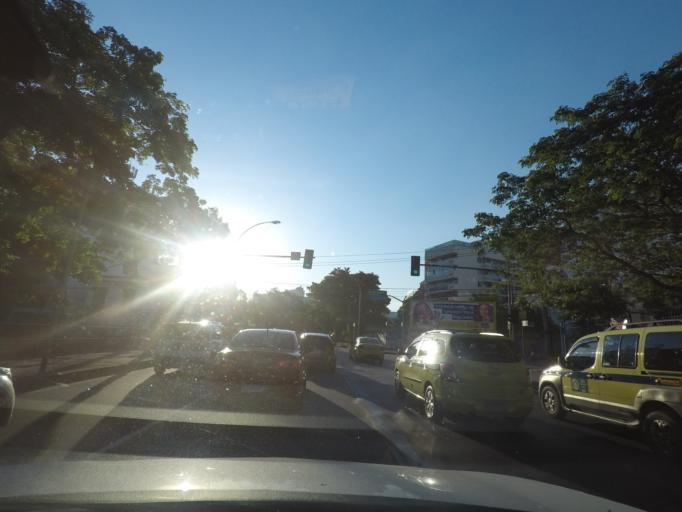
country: BR
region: Rio de Janeiro
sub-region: Rio De Janeiro
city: Rio de Janeiro
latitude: -22.9209
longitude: -43.2255
